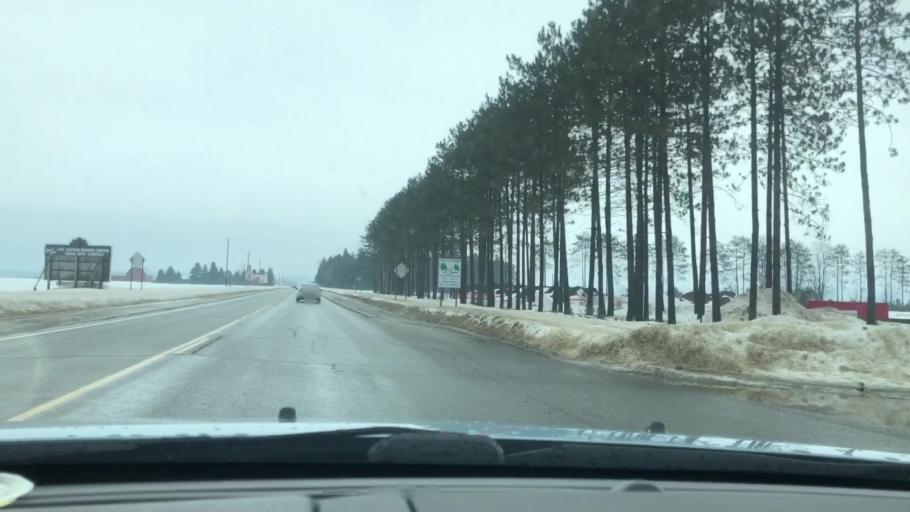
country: US
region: Michigan
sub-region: Charlevoix County
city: Boyne City
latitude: 45.0666
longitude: -84.8956
